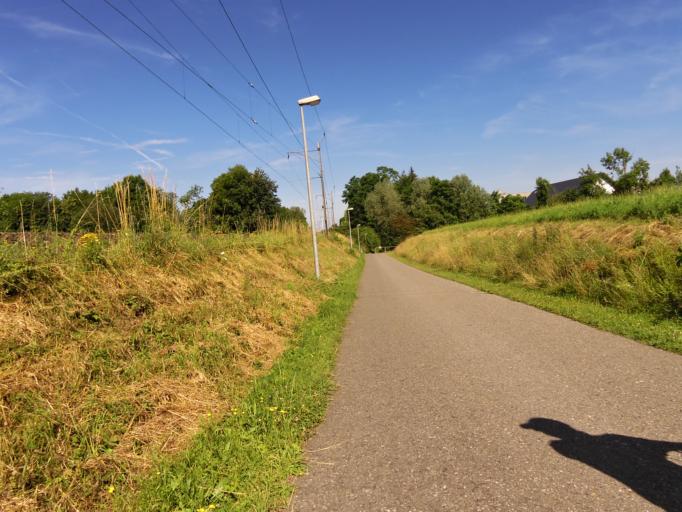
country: CH
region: Thurgau
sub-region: Kreuzlingen District
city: Bottighofen
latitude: 47.6415
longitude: 9.2116
